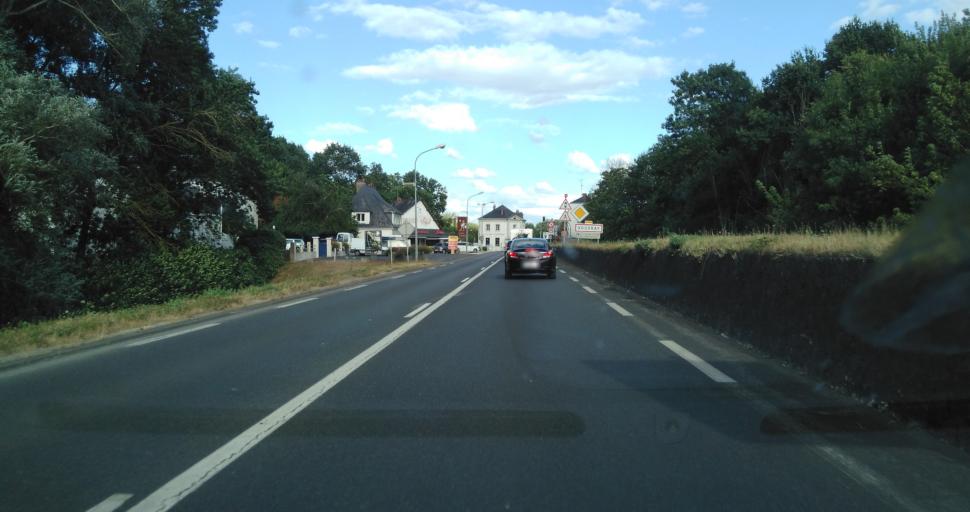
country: FR
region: Centre
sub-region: Departement d'Indre-et-Loire
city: Vouvray
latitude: 47.4100
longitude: 0.7946
